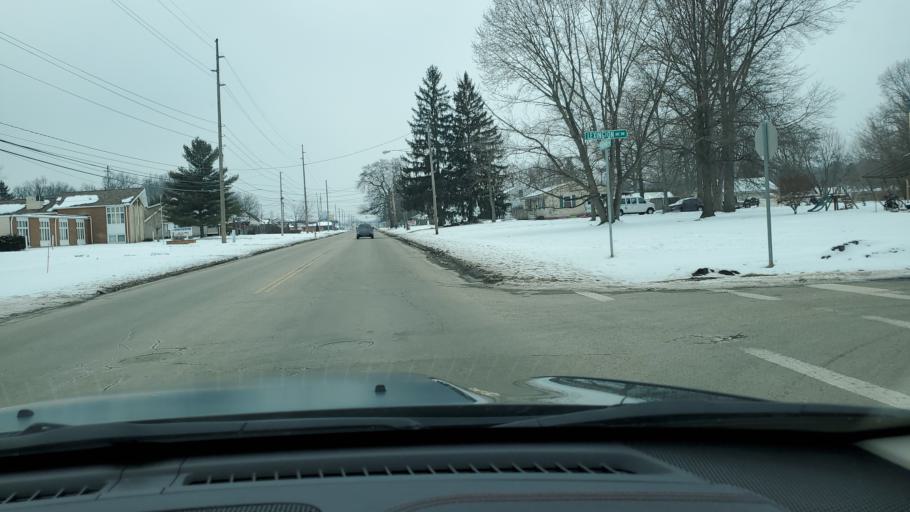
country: US
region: Ohio
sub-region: Trumbull County
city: Leavittsburg
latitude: 41.2472
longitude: -80.8472
